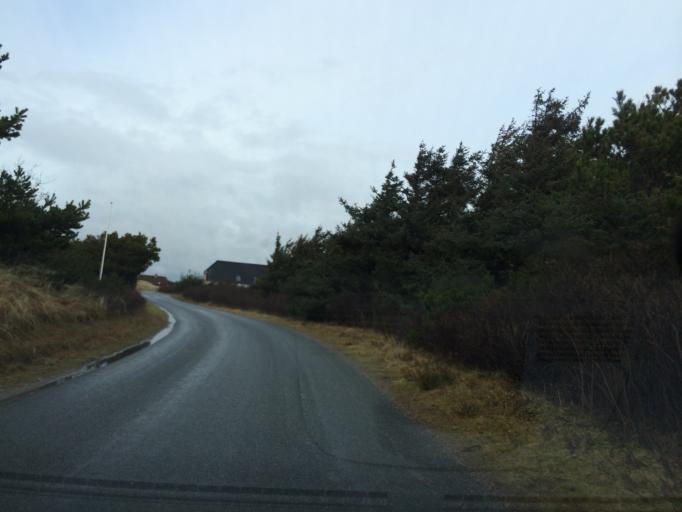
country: DK
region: Central Jutland
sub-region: Holstebro Kommune
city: Ulfborg
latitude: 56.2534
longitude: 8.1374
